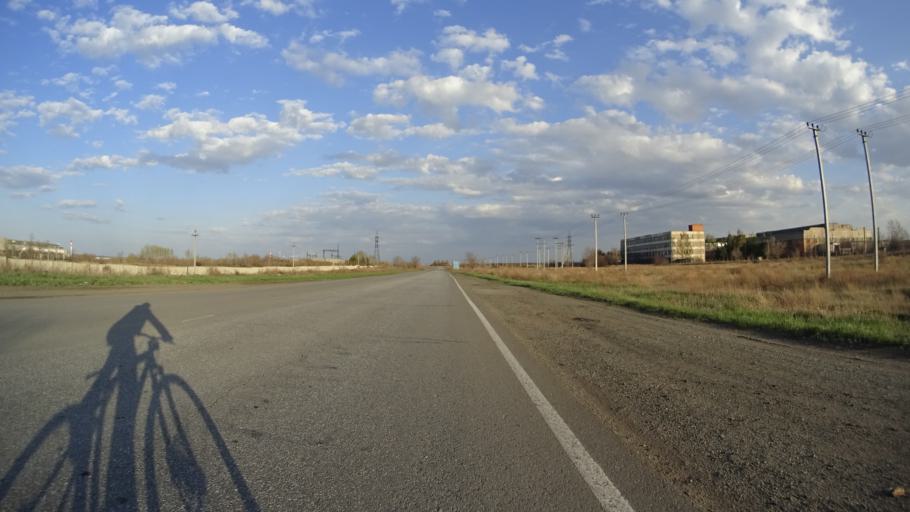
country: RU
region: Chelyabinsk
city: Troitsk
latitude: 54.0651
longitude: 61.5683
